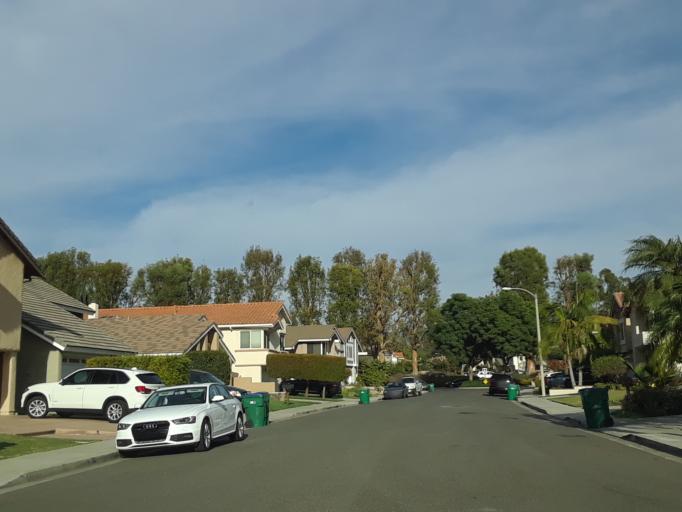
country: US
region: California
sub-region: Orange County
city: North Tustin
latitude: 33.7166
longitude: -117.7594
